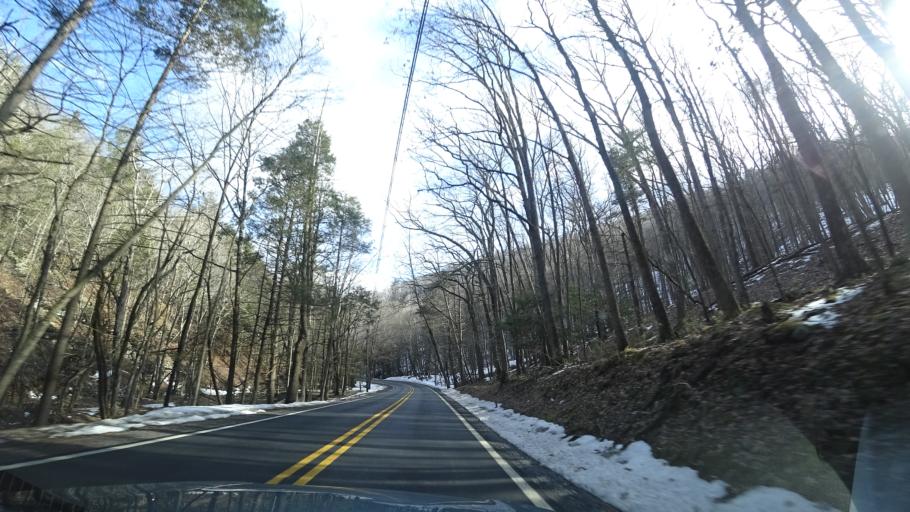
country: US
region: Virginia
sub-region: Shenandoah County
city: Basye
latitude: 38.8937
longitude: -78.9104
